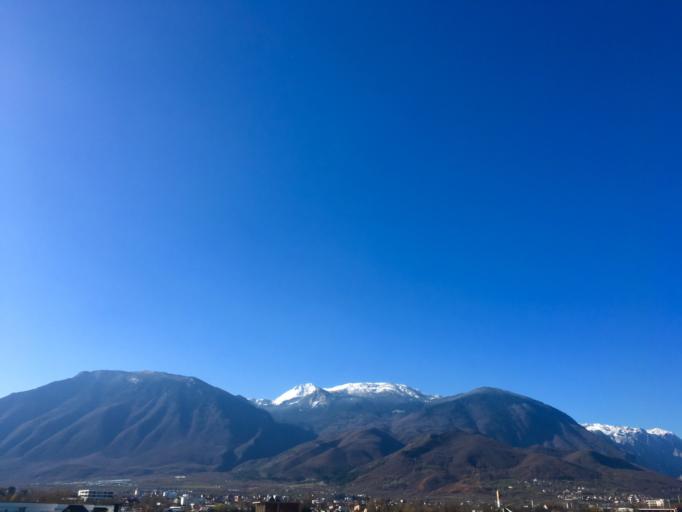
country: XK
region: Pec
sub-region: Komuna e Pejes
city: Peje
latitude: 42.6478
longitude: 20.3200
